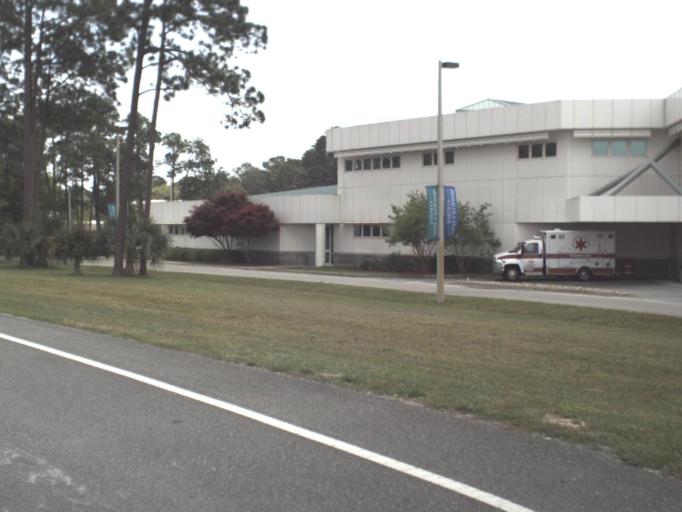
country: US
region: Florida
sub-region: Escambia County
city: Warrington
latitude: 30.3971
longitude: -87.2872
